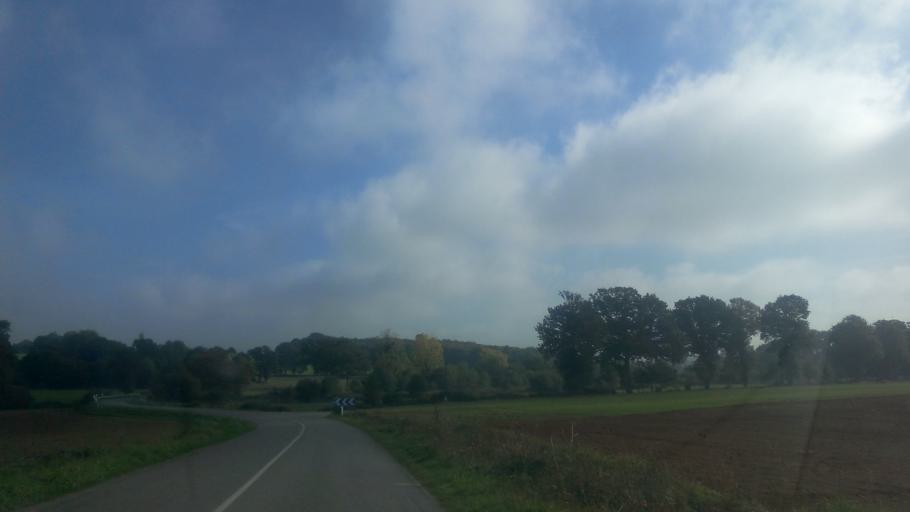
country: FR
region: Pays de la Loire
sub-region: Departement de la Loire-Atlantique
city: Conquereuil
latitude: 47.6253
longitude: -1.7702
